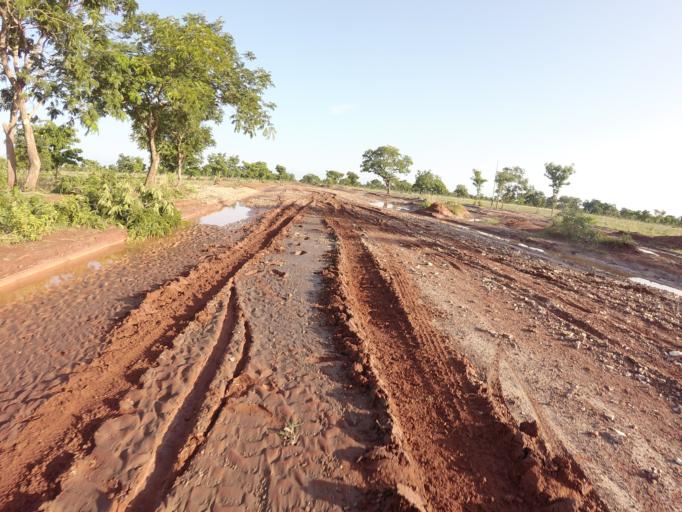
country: TG
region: Savanes
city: Sansanne-Mango
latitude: 10.3664
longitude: -0.0938
